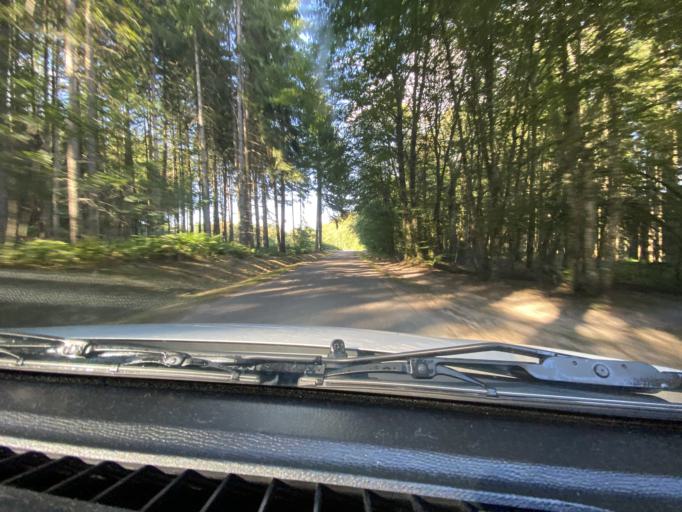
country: FR
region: Bourgogne
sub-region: Departement de la Cote-d'Or
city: Saulieu
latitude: 47.2959
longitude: 4.1741
